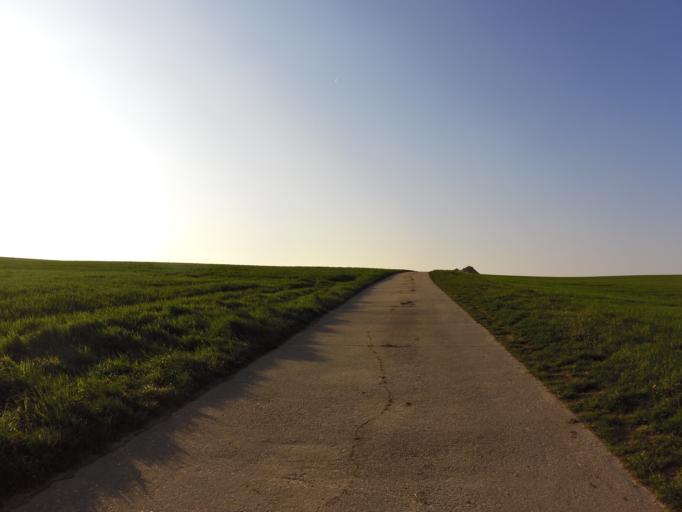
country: DE
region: Bavaria
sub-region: Regierungsbezirk Unterfranken
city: Theilheim
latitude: 49.7608
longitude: 10.0184
